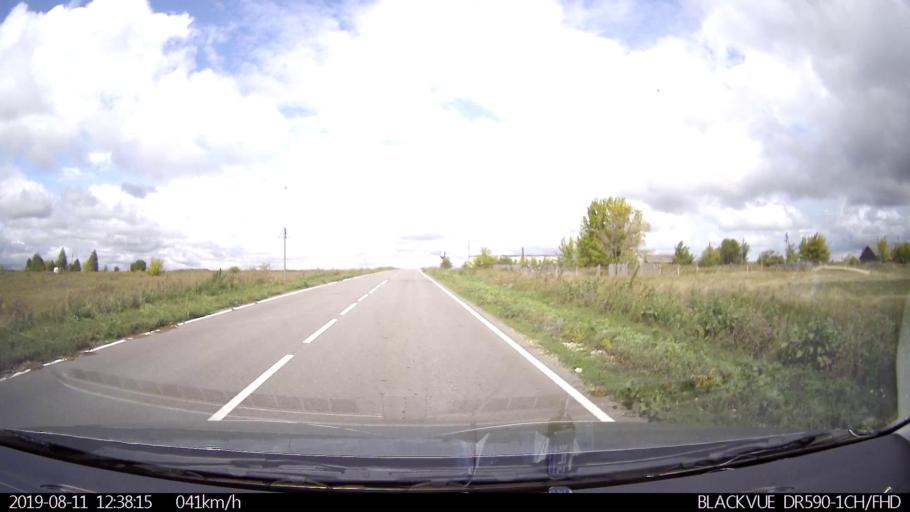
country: RU
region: Ulyanovsk
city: Ignatovka
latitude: 53.8257
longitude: 47.8080
